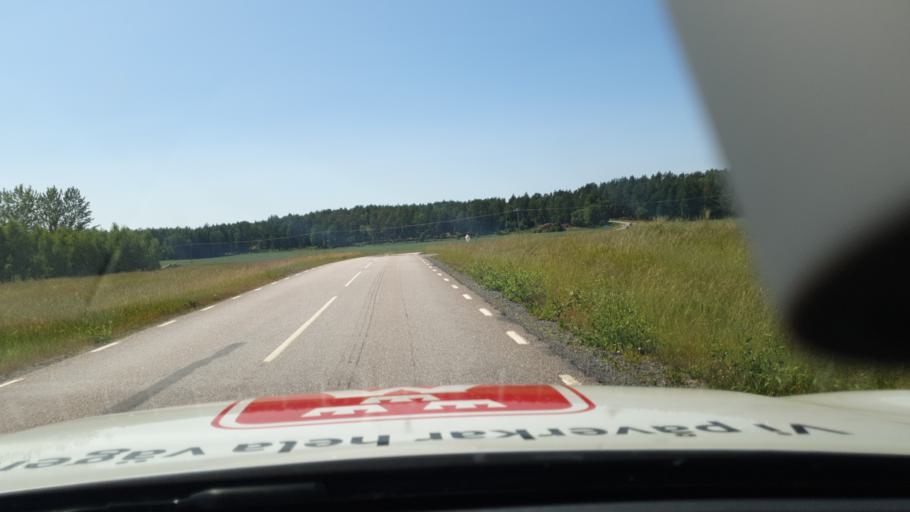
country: SE
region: Vaestra Goetaland
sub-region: Lidkopings Kommun
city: Lidkoping
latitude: 58.6630
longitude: 13.1911
